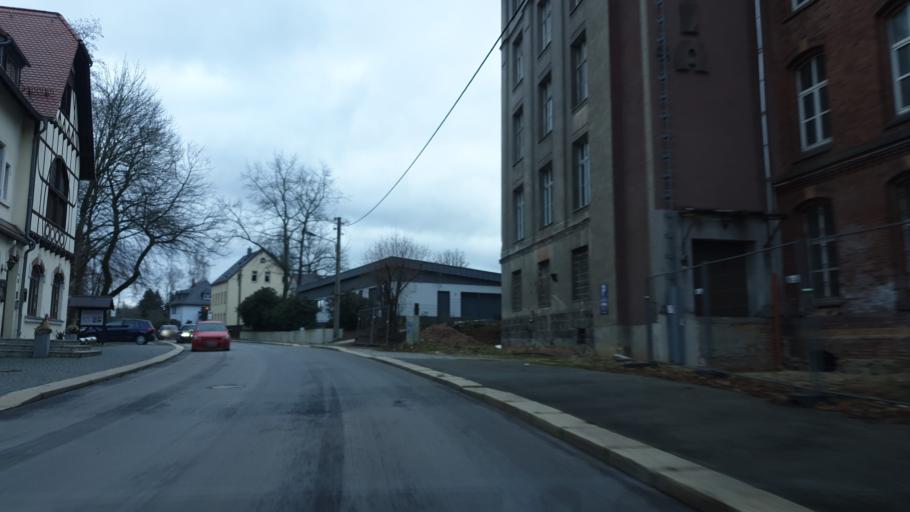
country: DE
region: Saxony
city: Lichtenstein
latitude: 50.7493
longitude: 12.6372
